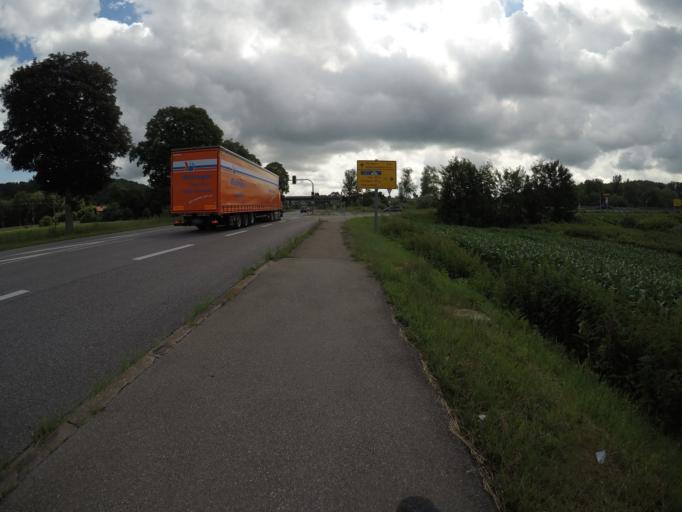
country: DE
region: Baden-Wuerttemberg
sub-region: Regierungsbezirk Stuttgart
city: Albershausen
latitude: 48.7169
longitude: 9.5567
